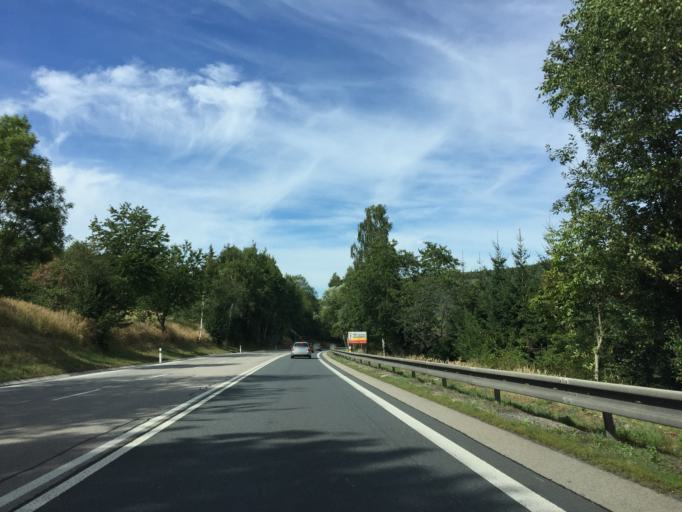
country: CZ
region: Central Bohemia
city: Votice
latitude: 49.6308
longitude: 14.6511
